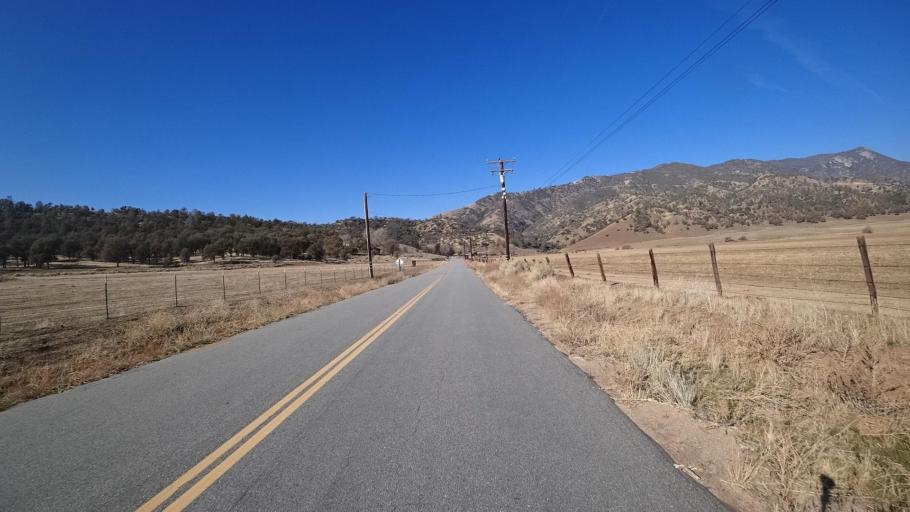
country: US
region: California
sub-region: Kern County
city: Bodfish
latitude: 35.3818
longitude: -118.5471
